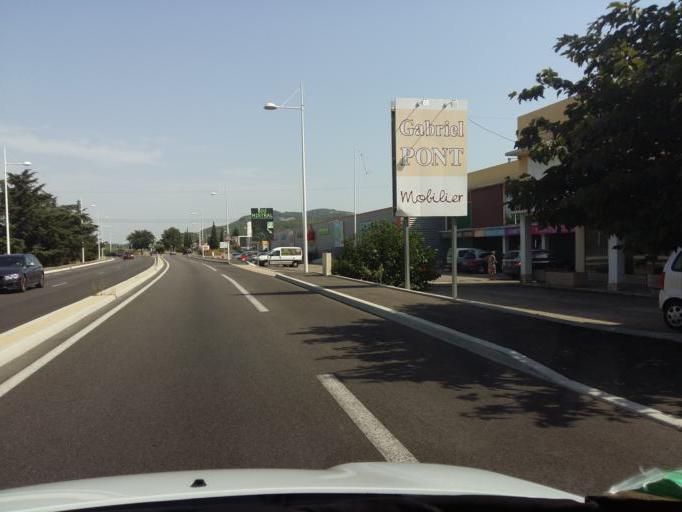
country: FR
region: Provence-Alpes-Cote d'Azur
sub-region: Departement du Vaucluse
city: Bollene
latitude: 44.2913
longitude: 4.7534
